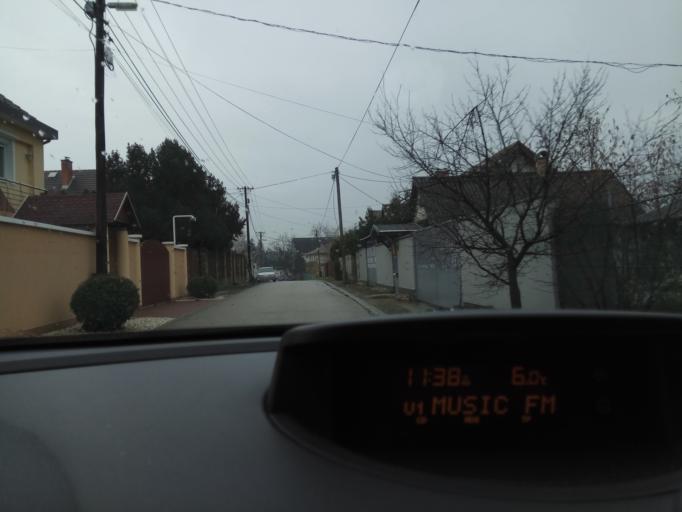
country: HU
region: Pest
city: Dunakeszi
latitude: 47.6090
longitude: 19.1304
